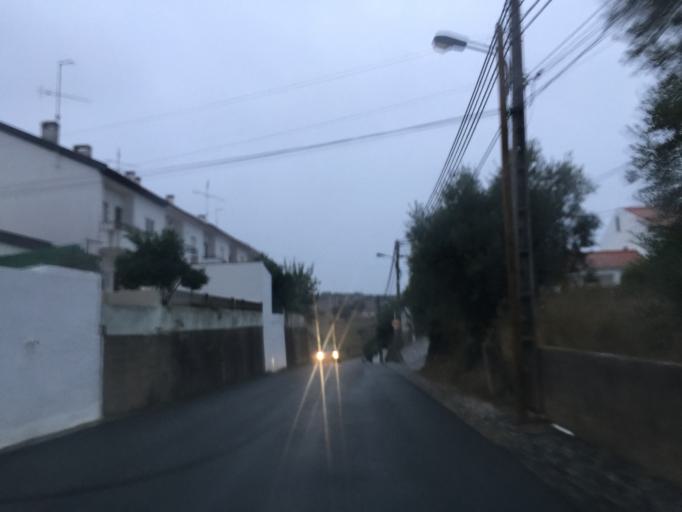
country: PT
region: Portalegre
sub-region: Avis
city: Avis
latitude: 39.0542
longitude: -7.8959
